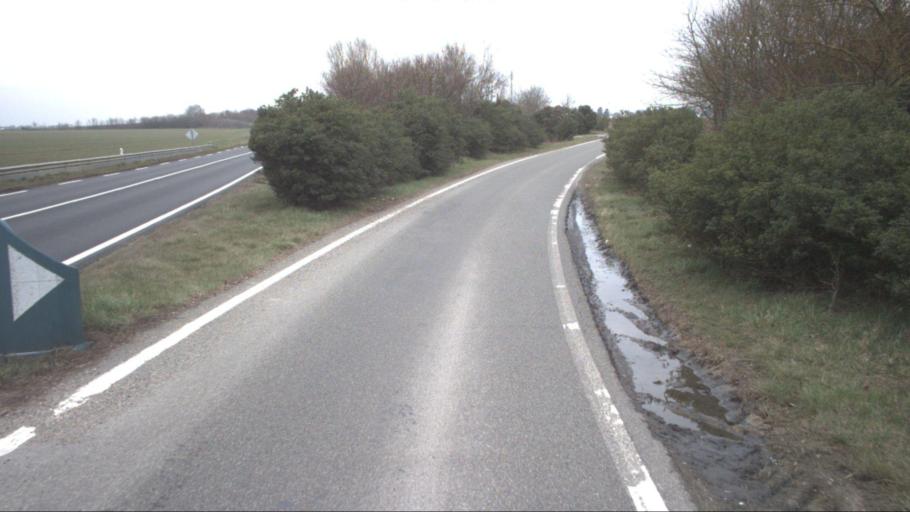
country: FR
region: Ile-de-France
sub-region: Departement des Yvelines
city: Ablis
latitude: 48.5054
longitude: 1.8366
